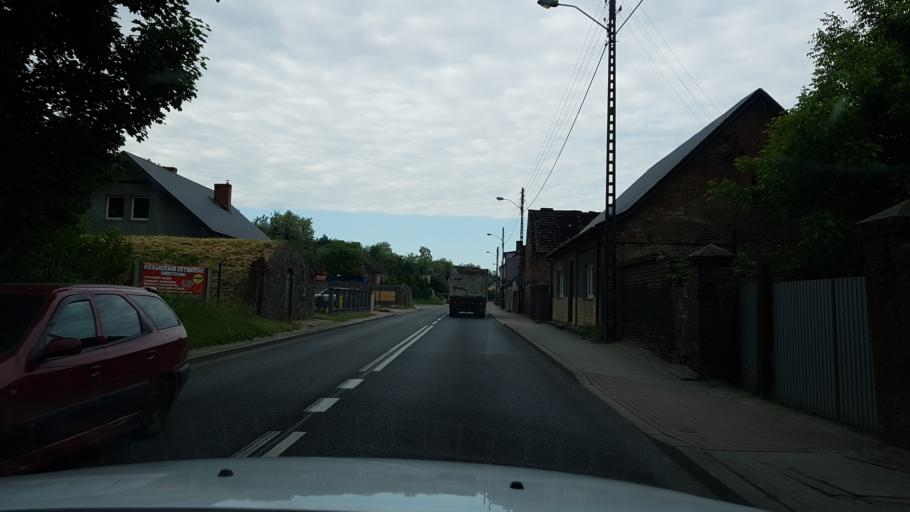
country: PL
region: West Pomeranian Voivodeship
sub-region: Powiat gryfinski
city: Gryfino
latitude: 53.2889
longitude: 14.5184
